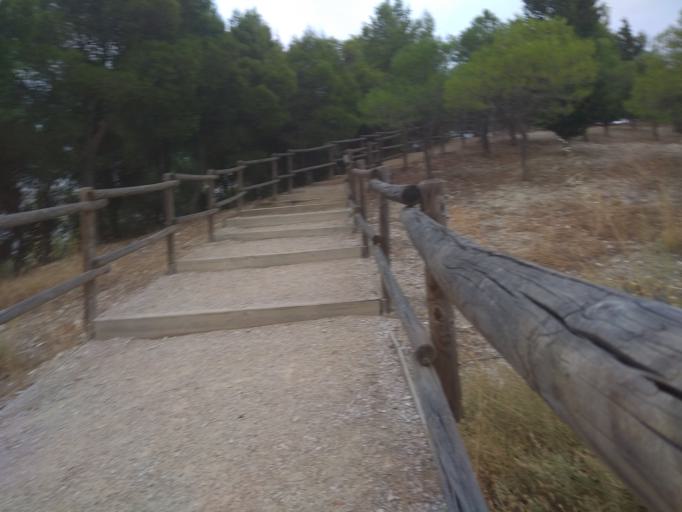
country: ES
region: Castille and Leon
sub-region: Provincia de Valladolid
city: Portillo
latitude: 41.4788
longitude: -4.5961
